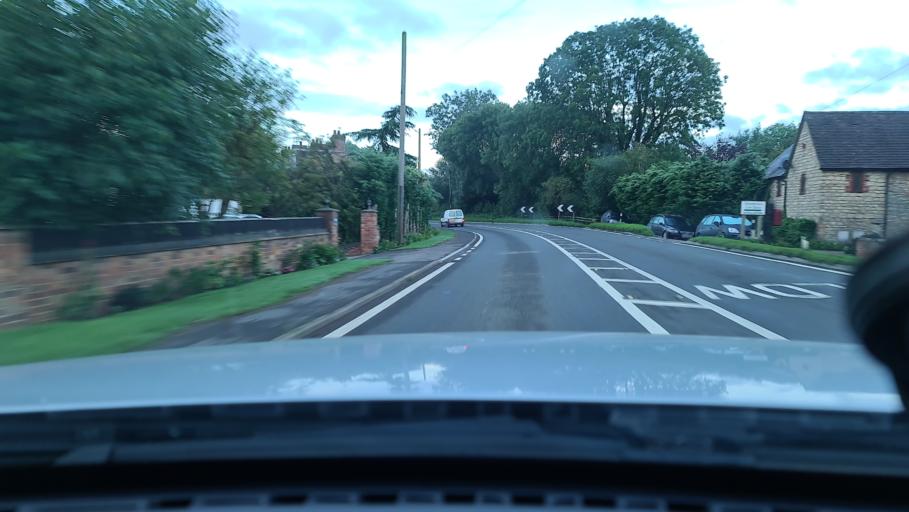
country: GB
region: England
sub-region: Warwickshire
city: Long Itchington
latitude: 52.2888
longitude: -1.3940
